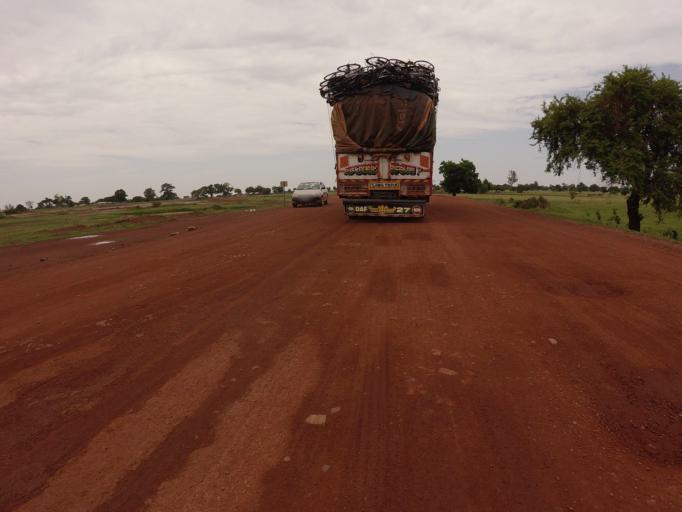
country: GH
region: Upper East
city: Bawku
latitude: 11.0024
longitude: -0.3791
